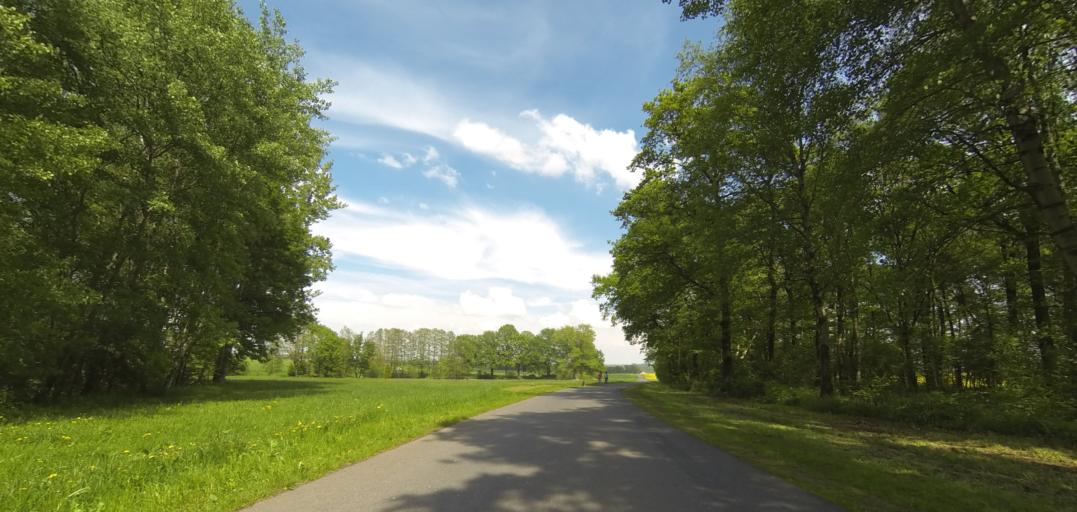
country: DE
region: Saxony
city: Arnsdorf
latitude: 51.0840
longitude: 13.9452
